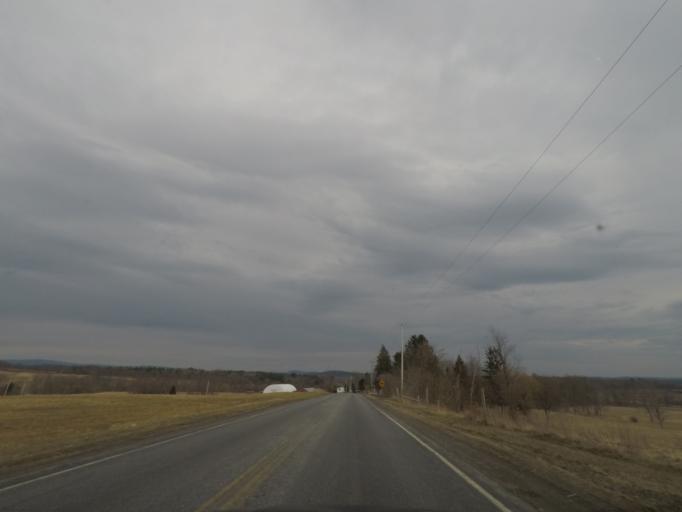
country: US
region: New York
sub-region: Washington County
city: Cambridge
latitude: 42.9663
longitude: -73.4649
